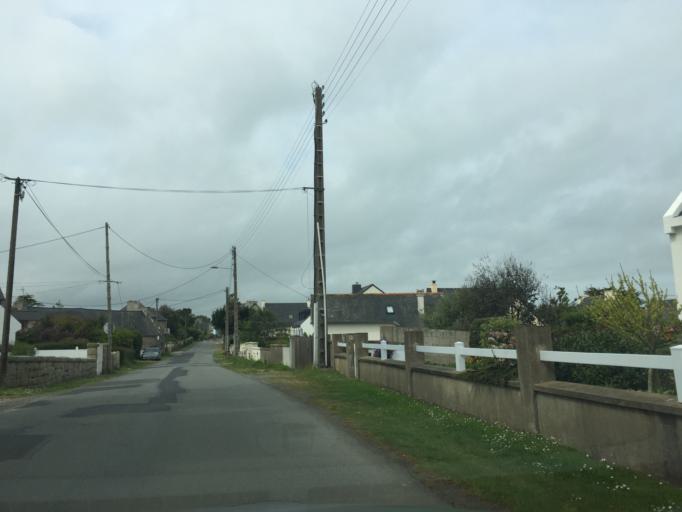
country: FR
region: Brittany
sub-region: Departement des Cotes-d'Armor
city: Saint-Cast-le-Guildo
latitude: 48.6417
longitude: -2.2523
